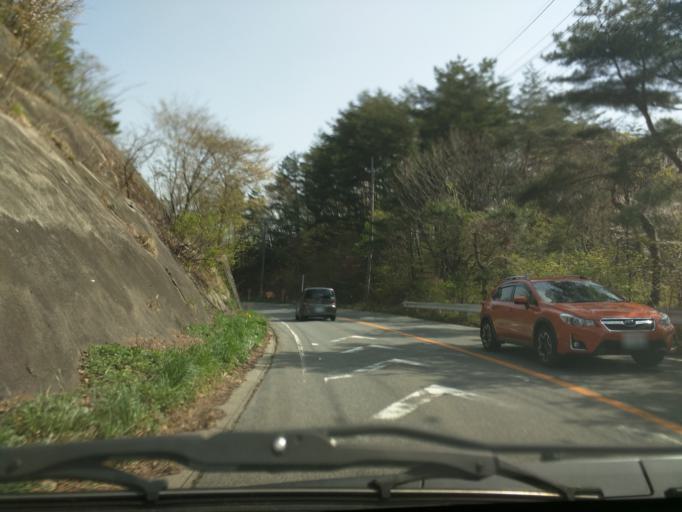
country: JP
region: Fukushima
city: Nihommatsu
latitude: 37.5961
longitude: 140.3673
